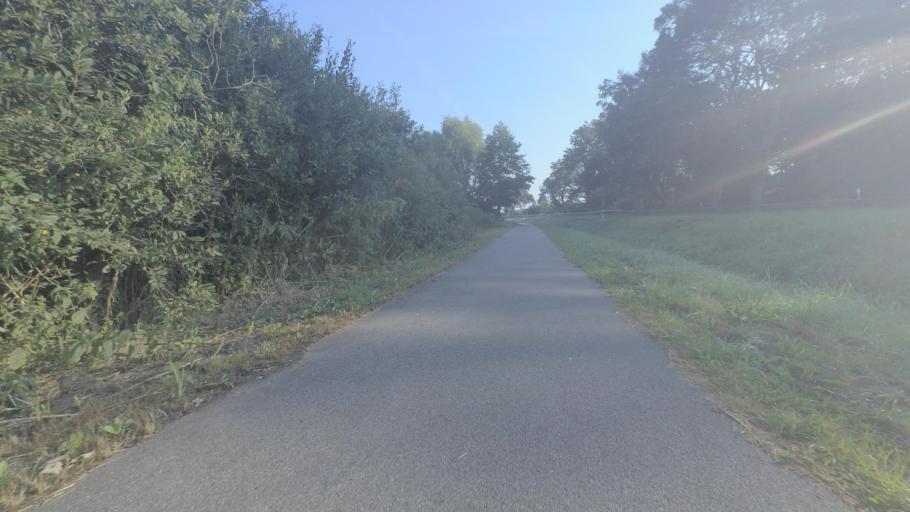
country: DE
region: Mecklenburg-Vorpommern
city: Tutow
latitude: 53.9843
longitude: 13.1510
